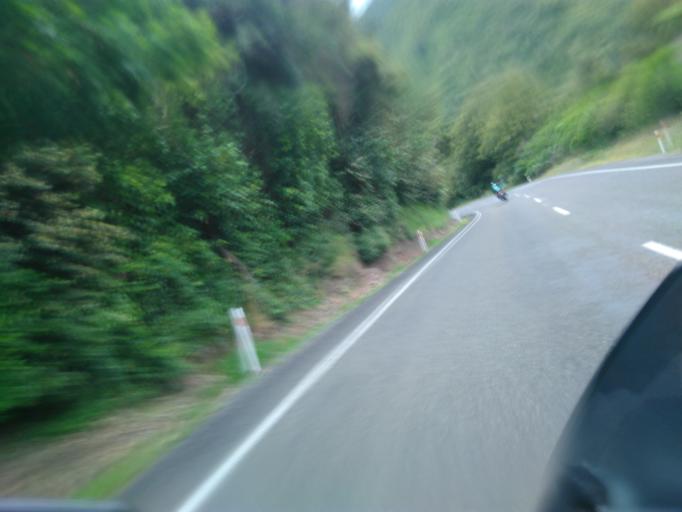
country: NZ
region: Bay of Plenty
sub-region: Opotiki District
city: Opotiki
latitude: -38.2364
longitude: 177.3097
